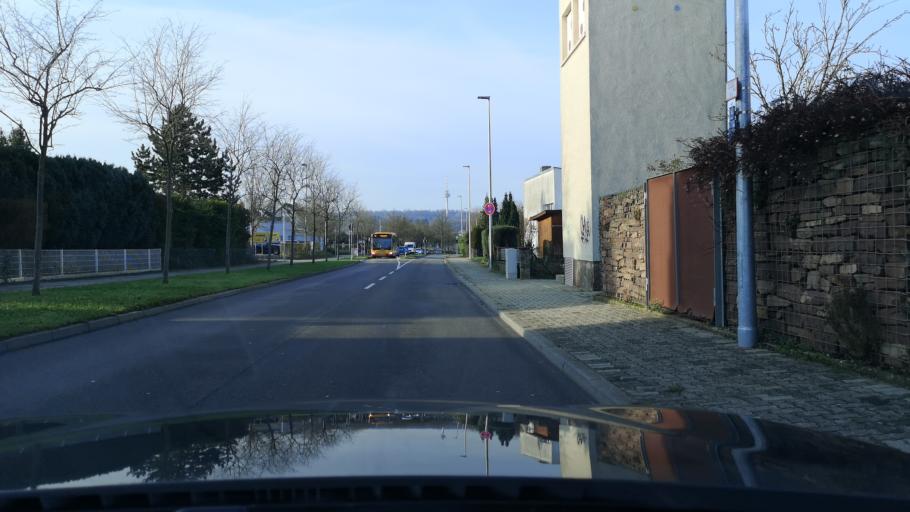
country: DE
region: Baden-Wuerttemberg
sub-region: Karlsruhe Region
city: Ettlingen
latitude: 48.9469
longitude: 8.4797
